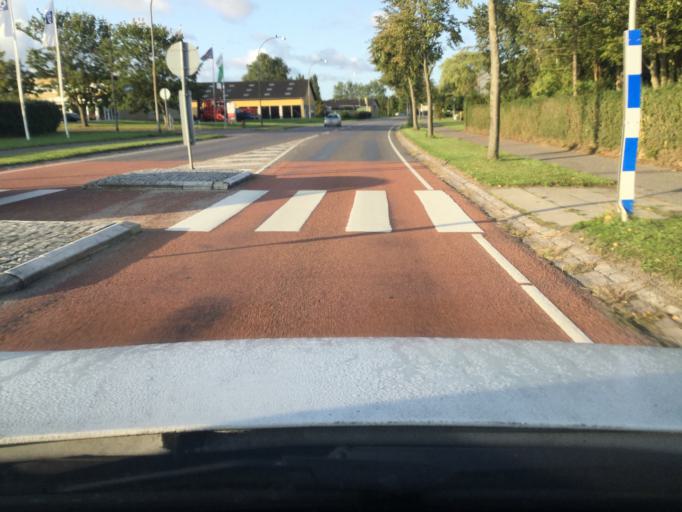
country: DK
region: Zealand
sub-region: Lolland Kommune
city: Nakskov
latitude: 54.8266
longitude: 11.1612
